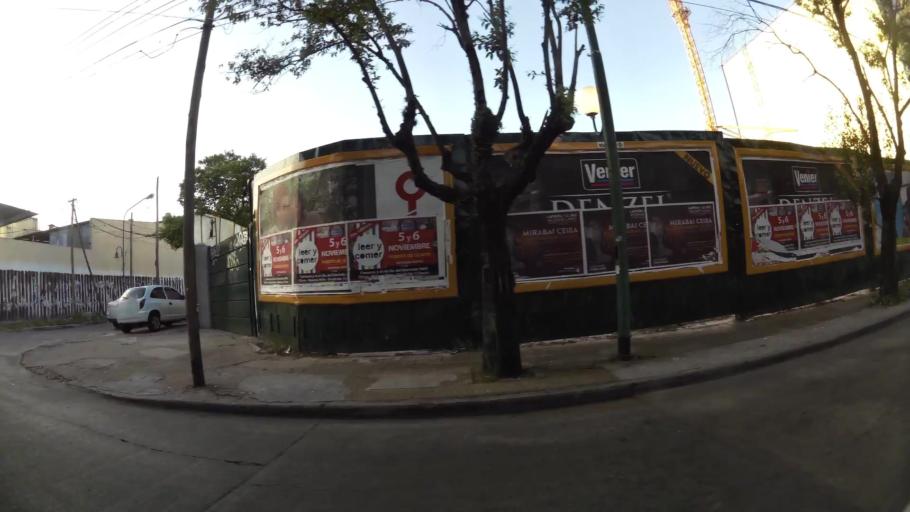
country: AR
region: Buenos Aires
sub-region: Partido de General San Martin
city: General San Martin
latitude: -34.5453
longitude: -58.4984
